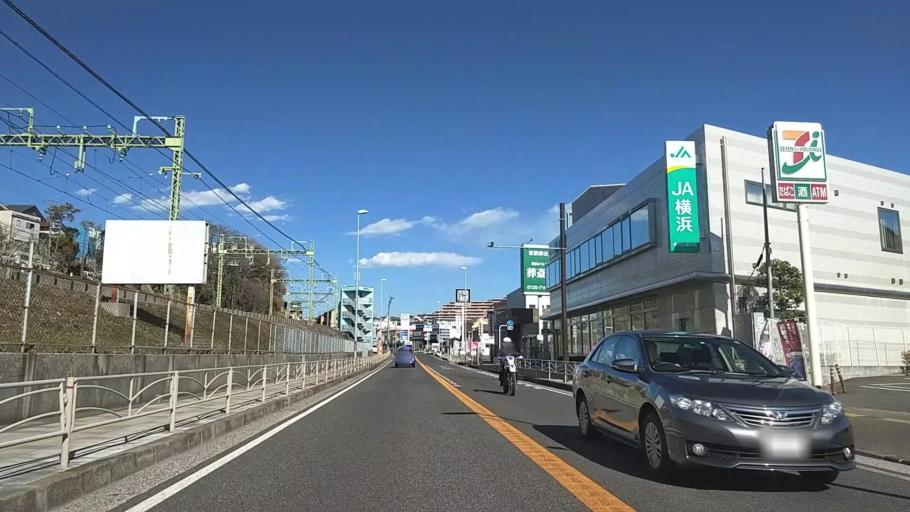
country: JP
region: Kanagawa
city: Zushi
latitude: 35.3502
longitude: 139.6258
